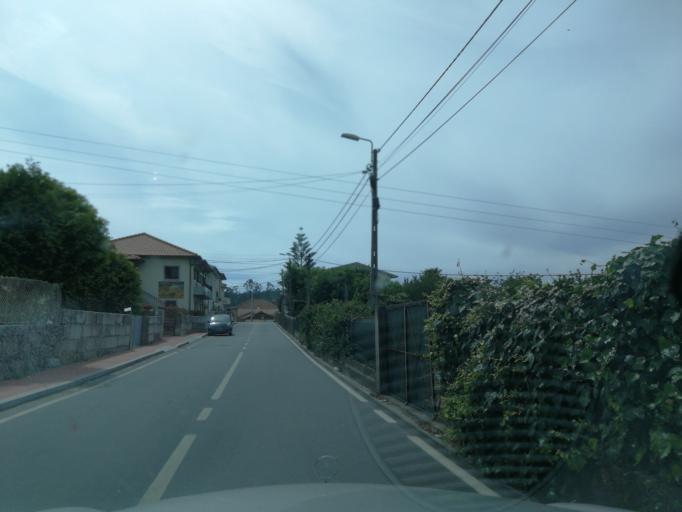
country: PT
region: Braga
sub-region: Vila Nova de Famalicao
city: Calendario
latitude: 41.4096
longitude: -8.5342
